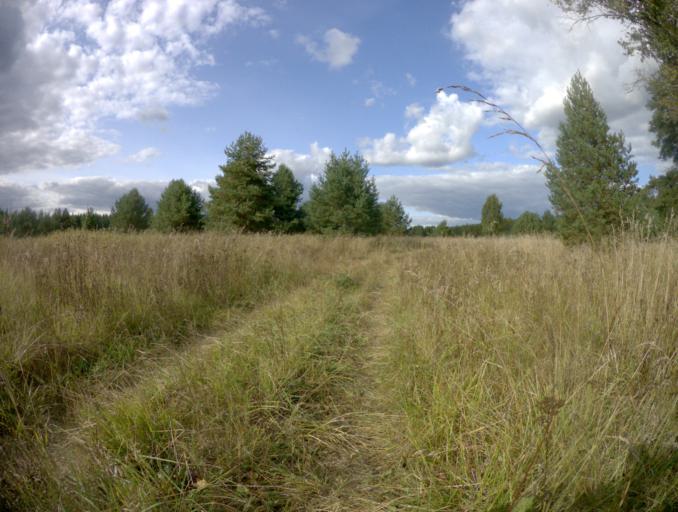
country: RU
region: Vladimir
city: Ivanishchi
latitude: 55.8541
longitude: 40.3969
